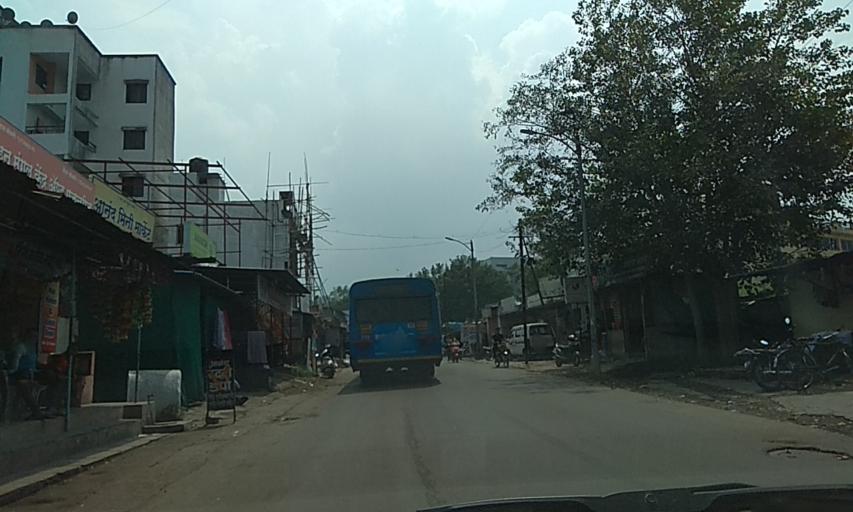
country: IN
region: Maharashtra
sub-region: Pune Division
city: Shivaji Nagar
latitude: 18.5400
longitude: 73.7939
